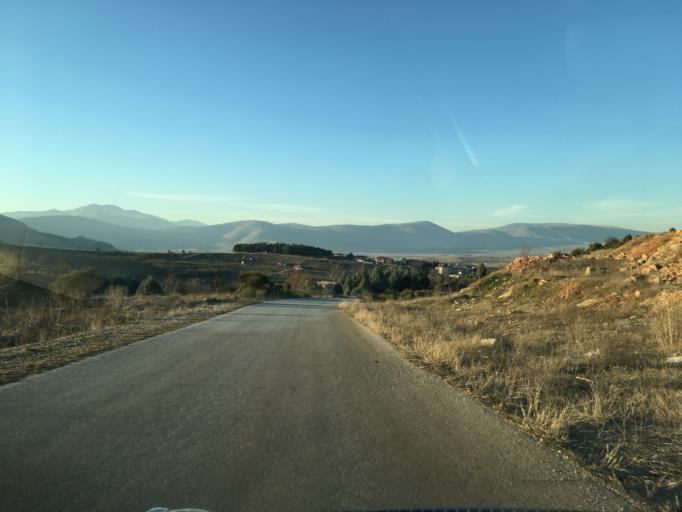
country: GR
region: West Macedonia
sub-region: Nomos Kozanis
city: Kozani
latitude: 40.2796
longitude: 21.7335
